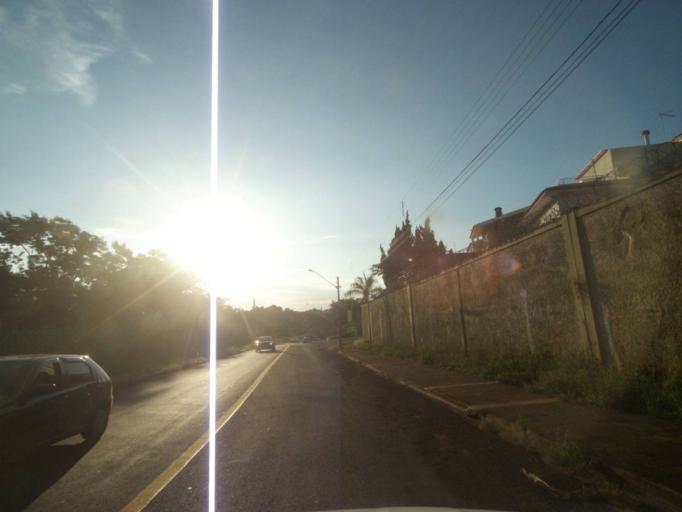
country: BR
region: Parana
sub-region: Londrina
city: Londrina
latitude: -23.3495
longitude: -51.1921
